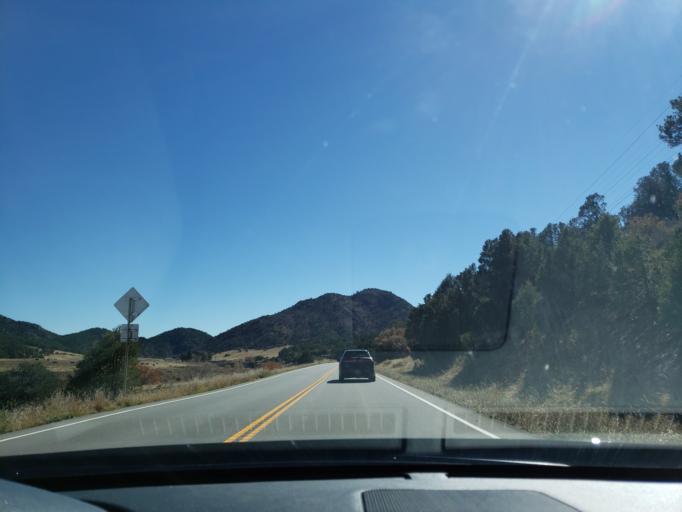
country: US
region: Colorado
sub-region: Fremont County
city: Canon City
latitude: 38.5898
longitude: -105.4235
